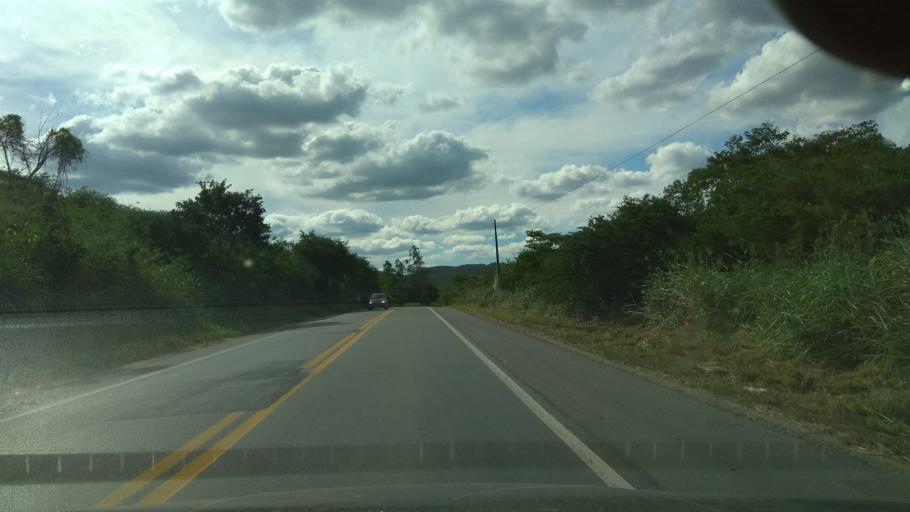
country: BR
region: Bahia
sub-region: Jequie
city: Jequie
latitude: -13.9050
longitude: -40.0178
